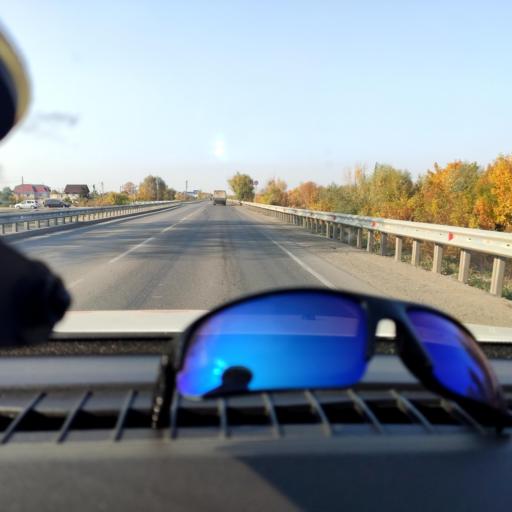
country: RU
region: Samara
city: Samara
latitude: 53.1178
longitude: 50.1224
